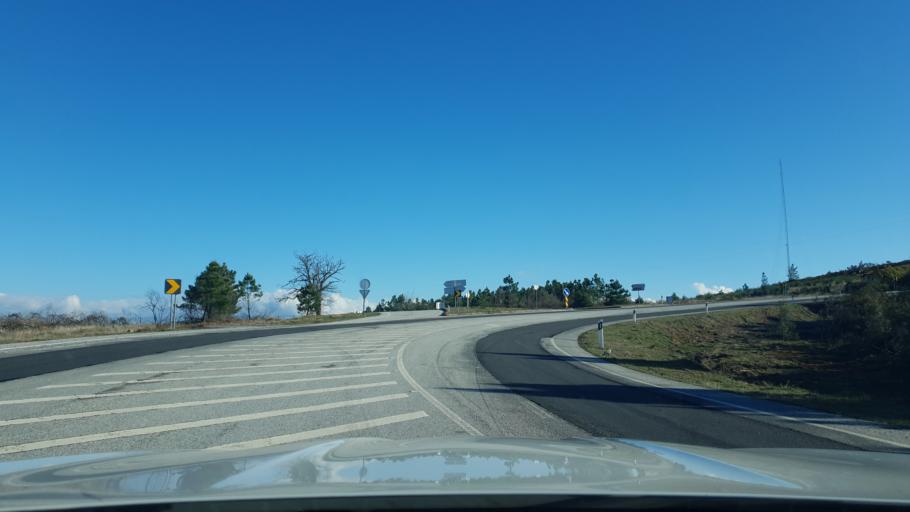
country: PT
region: Braganca
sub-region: Freixo de Espada A Cinta
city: Freixo de Espada a Cinta
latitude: 41.1549
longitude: -6.7979
